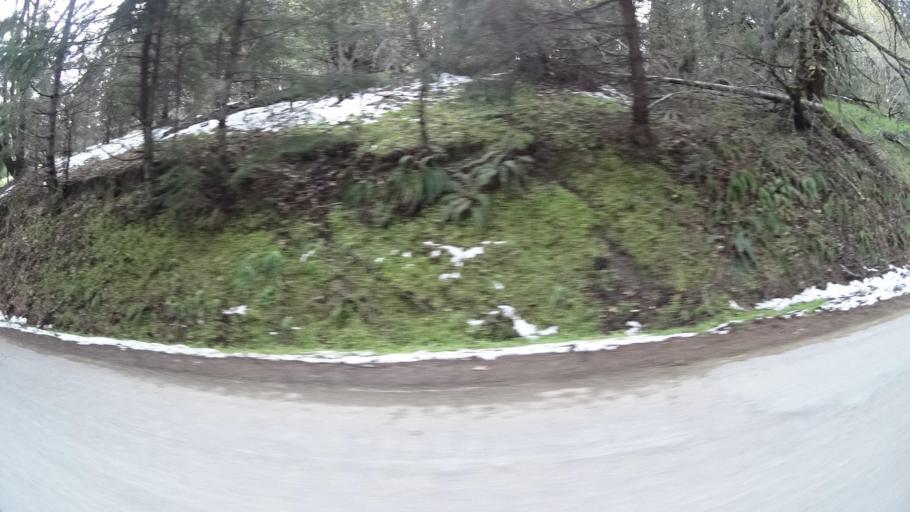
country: US
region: California
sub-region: Humboldt County
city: Willow Creek
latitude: 40.8849
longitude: -123.7715
